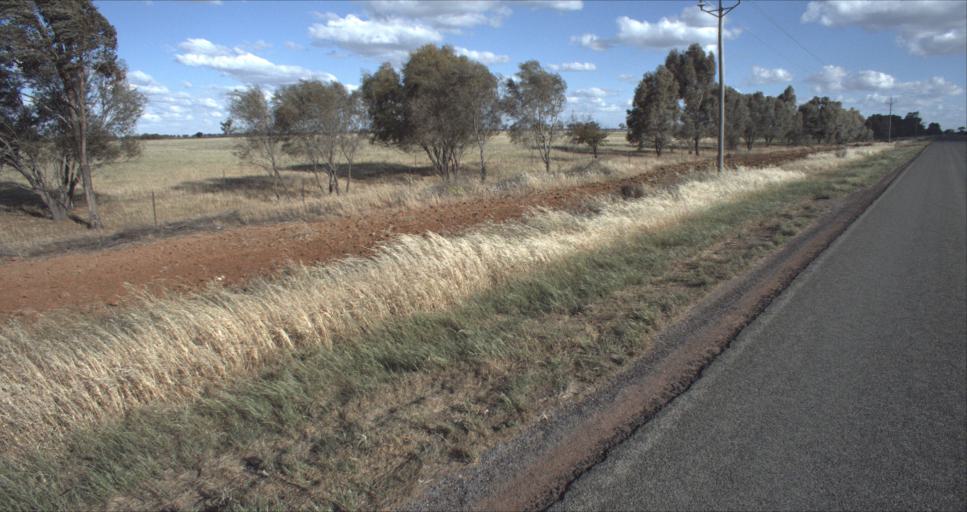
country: AU
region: New South Wales
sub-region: Leeton
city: Leeton
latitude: -34.5299
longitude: 146.2817
